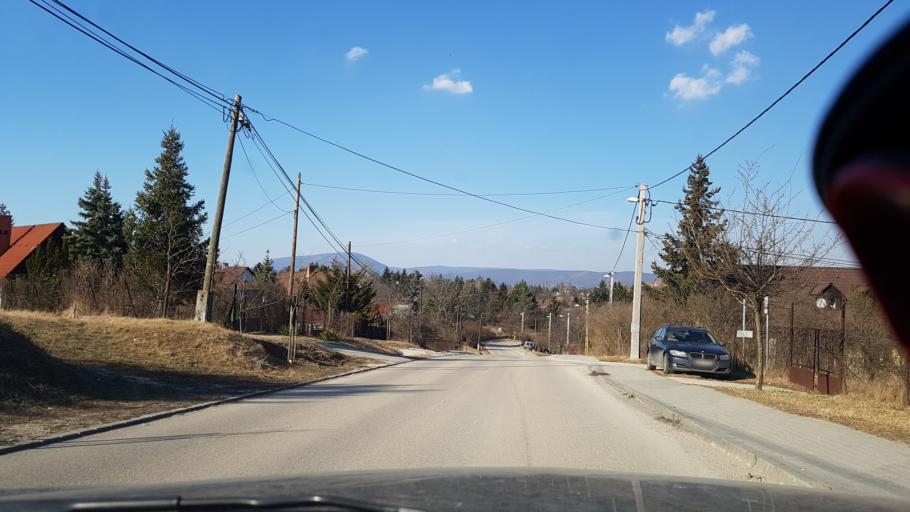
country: HU
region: Pest
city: Solymar
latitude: 47.5935
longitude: 18.9198
